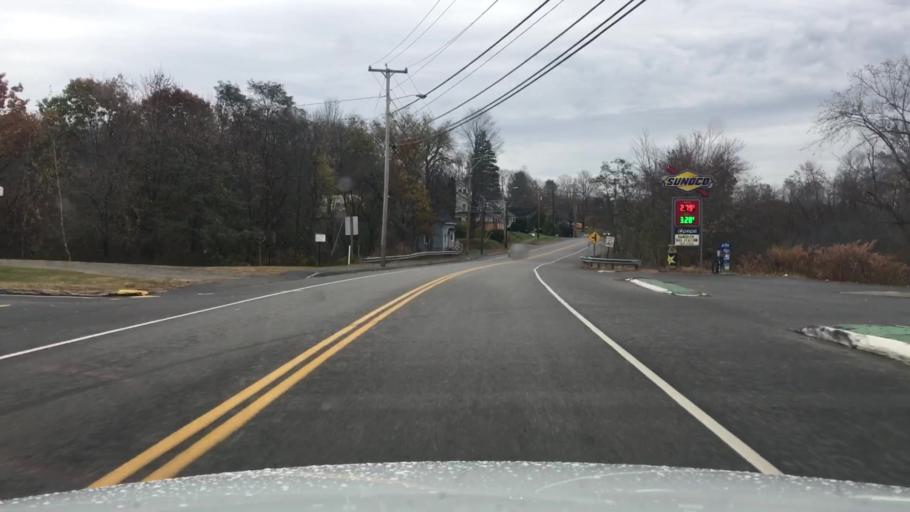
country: US
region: Maine
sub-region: Kennebec County
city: Randolph
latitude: 44.2287
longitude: -69.7649
